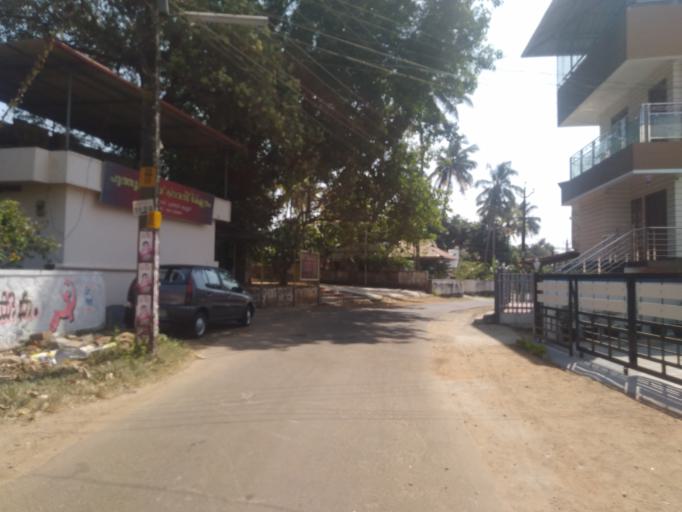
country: IN
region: Kerala
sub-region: Thrissur District
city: Trichur
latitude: 10.4868
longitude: 76.2831
